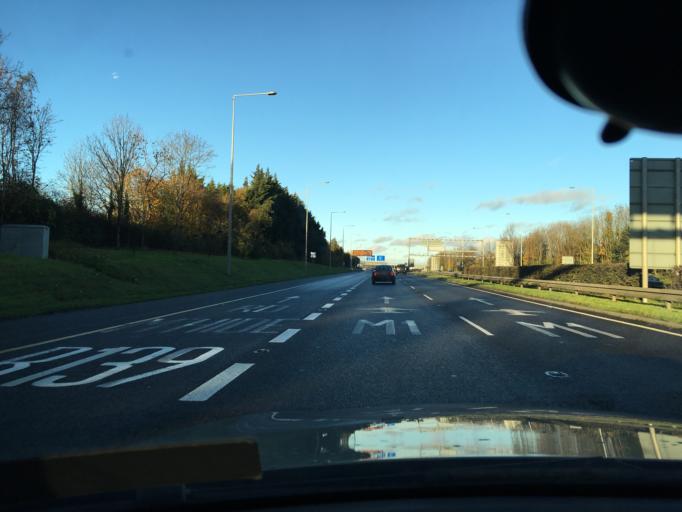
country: IE
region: Leinster
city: Beaumont
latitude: 53.4033
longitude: -6.2331
